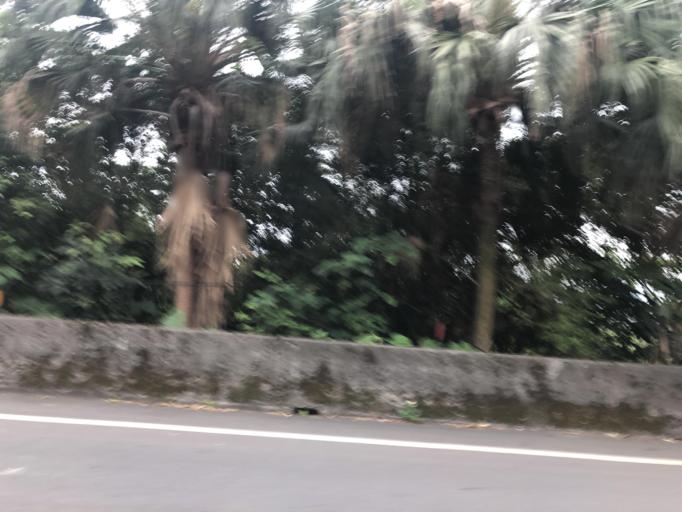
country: TW
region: Taiwan
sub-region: Keelung
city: Keelung
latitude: 25.1935
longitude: 121.6809
